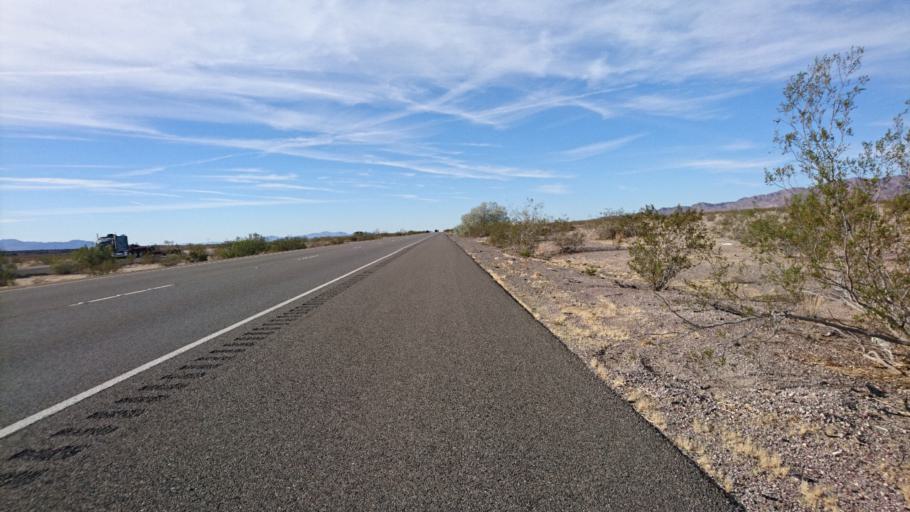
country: US
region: California
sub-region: San Bernardino County
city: Fort Irwin
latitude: 34.7590
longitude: -116.3469
